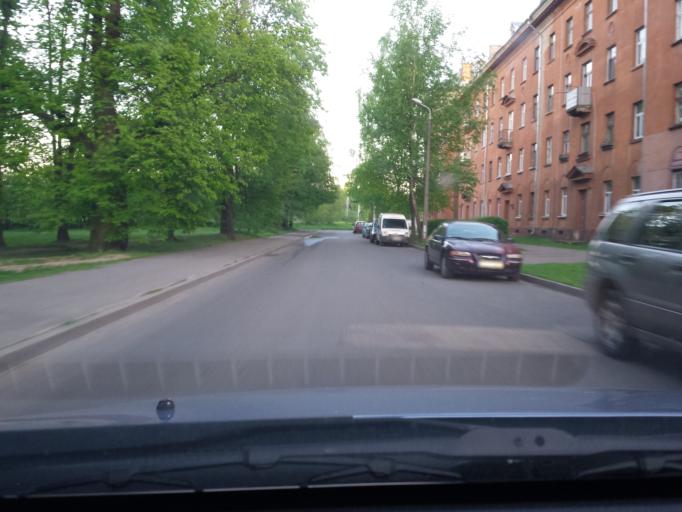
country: LV
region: Riga
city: Riga
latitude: 56.9883
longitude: 24.1373
